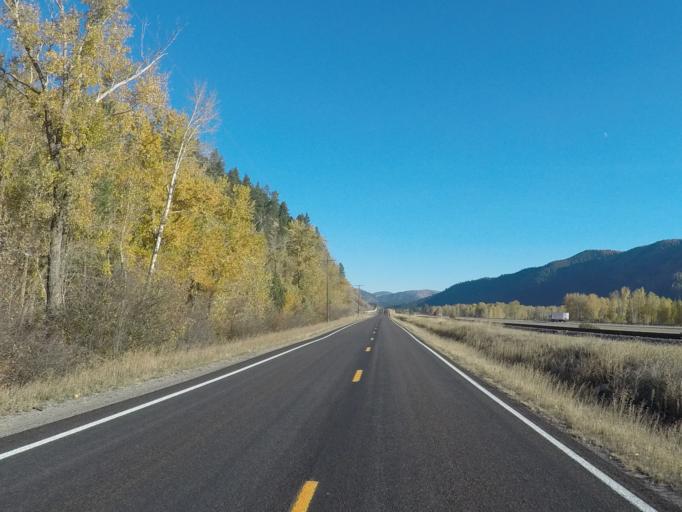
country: US
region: Montana
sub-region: Missoula County
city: Clinton
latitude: 46.8155
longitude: -113.7928
